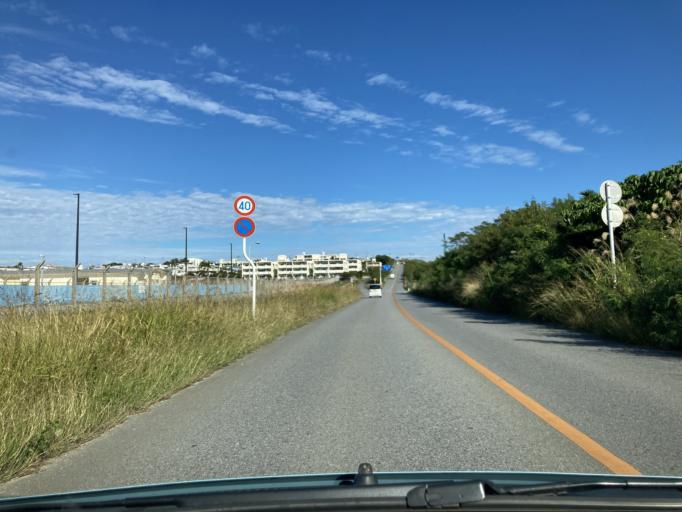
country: JP
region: Okinawa
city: Okinawa
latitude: 26.3772
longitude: 127.7456
